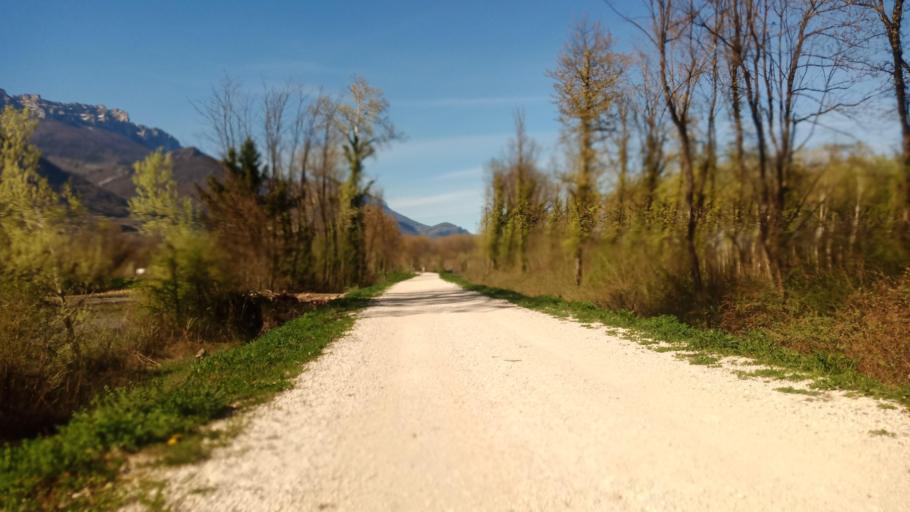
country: FR
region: Rhone-Alpes
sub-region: Departement de l'Isere
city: Le Champ-pres-Froges
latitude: 45.2978
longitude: 5.9327
